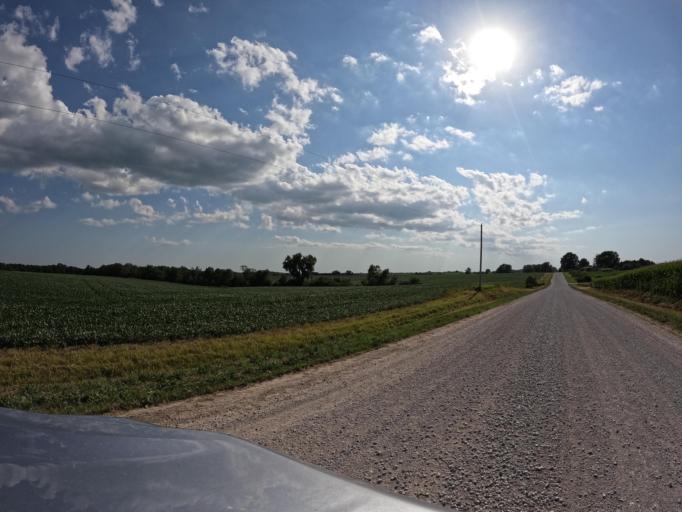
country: US
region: Iowa
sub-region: Appanoose County
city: Centerville
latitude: 40.7178
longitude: -93.0143
